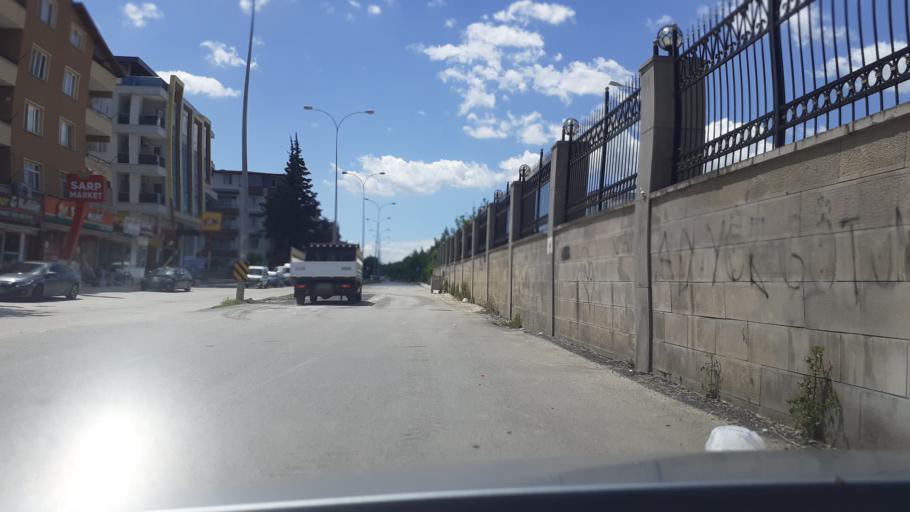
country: TR
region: Hatay
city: Anayazi
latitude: 36.3372
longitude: 36.2002
